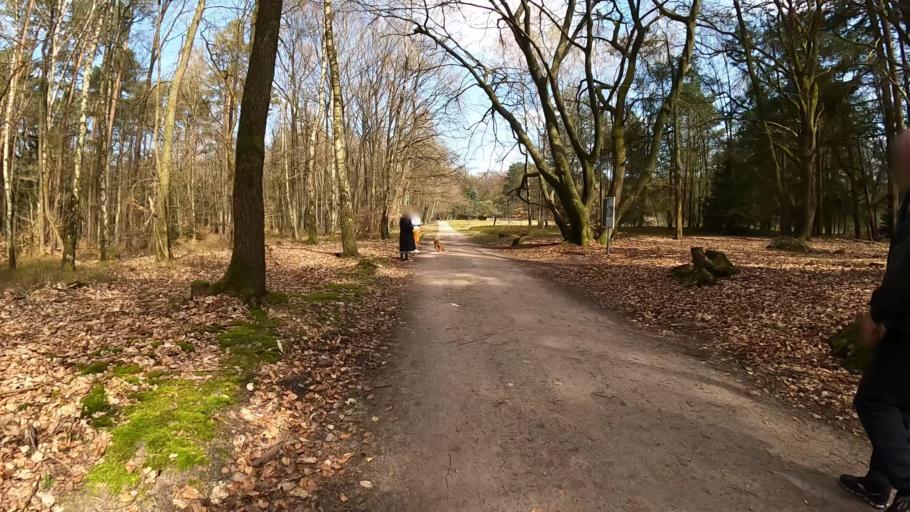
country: DE
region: Lower Saxony
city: Neu Wulmstorf
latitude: 53.4420
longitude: 9.8522
